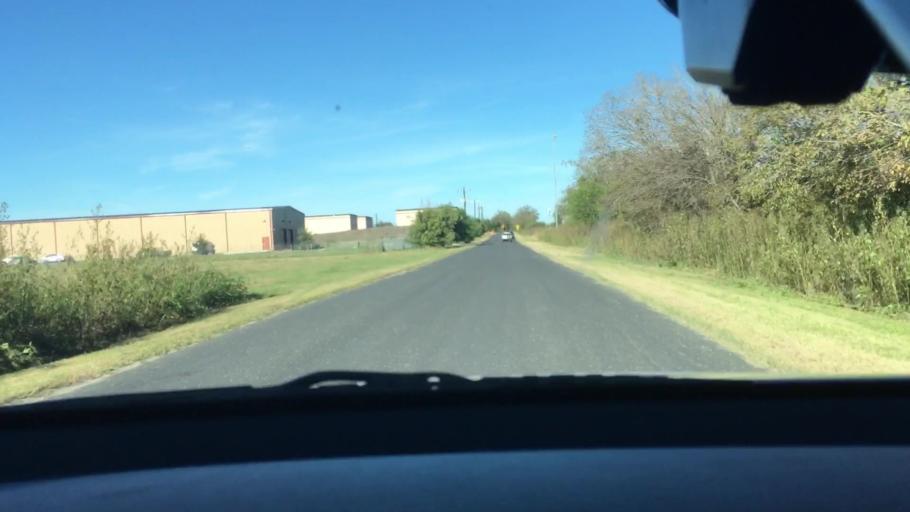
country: US
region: Texas
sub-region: Bexar County
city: Converse
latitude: 29.5231
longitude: -98.3106
